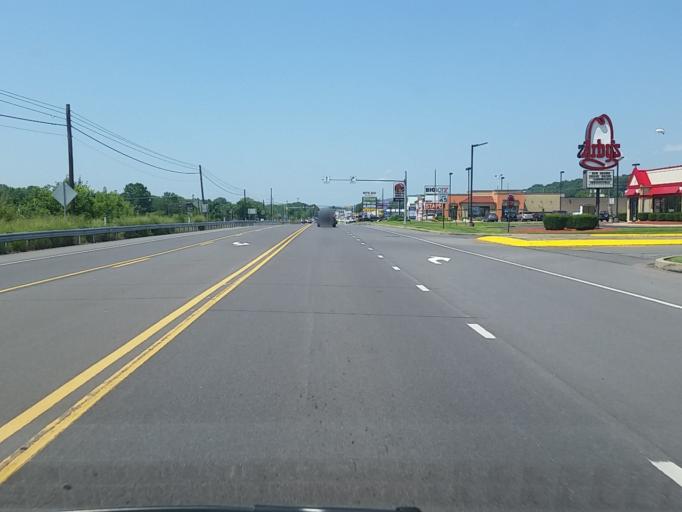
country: US
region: Pennsylvania
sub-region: Columbia County
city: Espy
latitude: 41.0120
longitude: -76.4109
